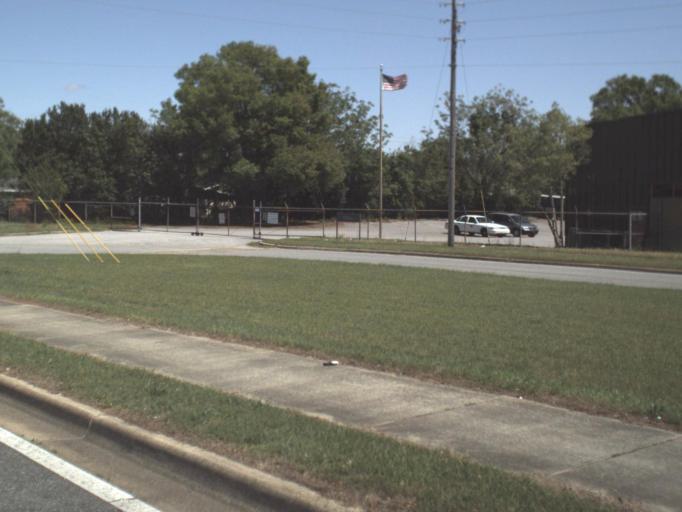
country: US
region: Florida
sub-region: Escambia County
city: Goulding
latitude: 30.4461
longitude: -87.2222
